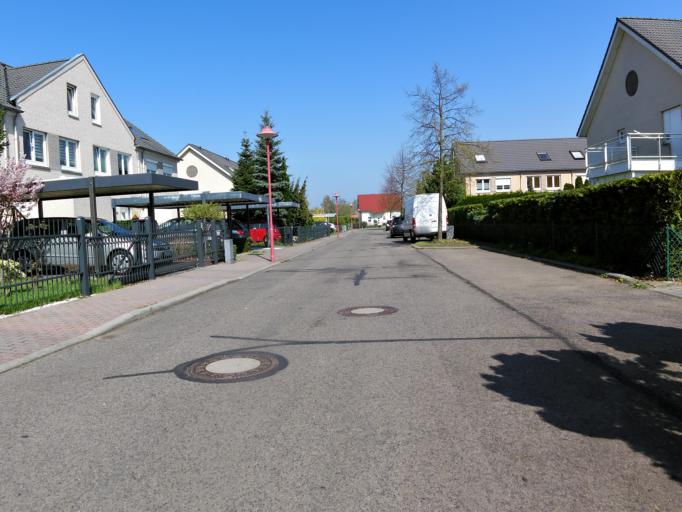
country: DE
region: Saxony
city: Leipzig
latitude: 51.3902
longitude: 12.3315
